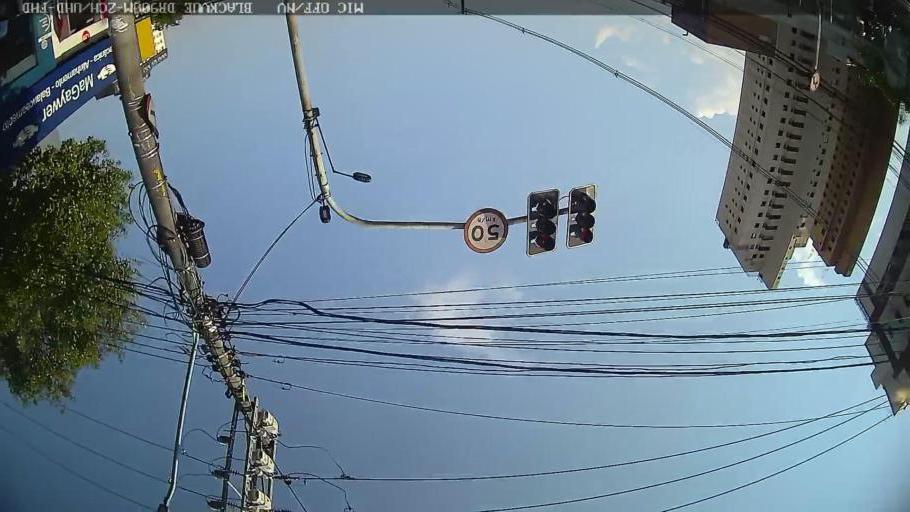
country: BR
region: Sao Paulo
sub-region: Taboao Da Serra
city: Taboao da Serra
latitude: -23.6087
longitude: -46.7260
